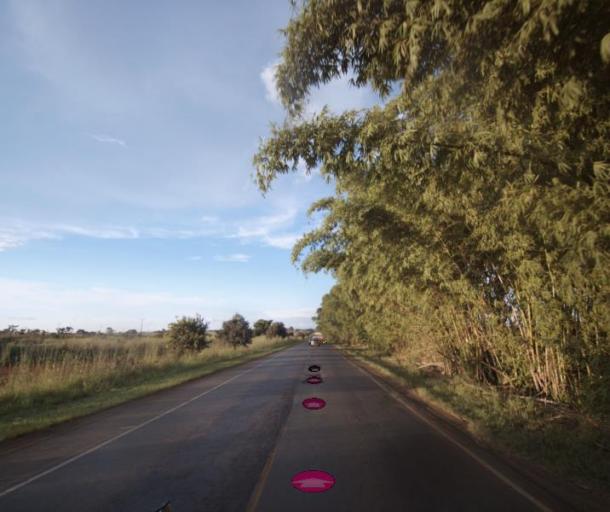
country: BR
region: Goias
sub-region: Anapolis
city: Anapolis
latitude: -16.2204
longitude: -48.9223
